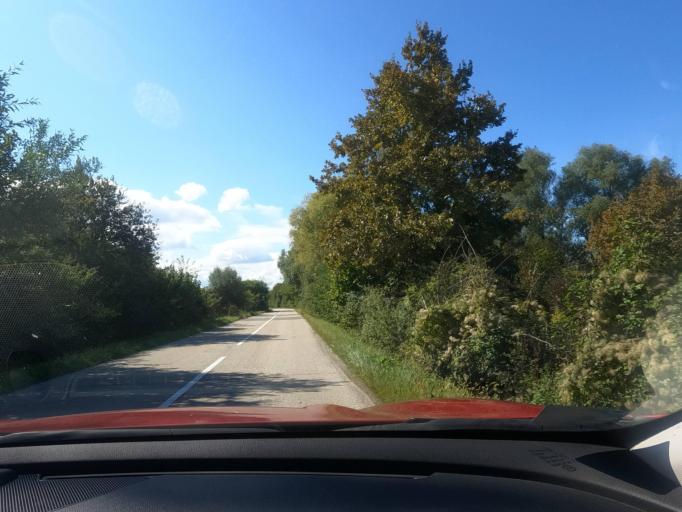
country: BA
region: Federation of Bosnia and Herzegovina
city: Vrnograc
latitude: 45.2510
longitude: 15.9432
